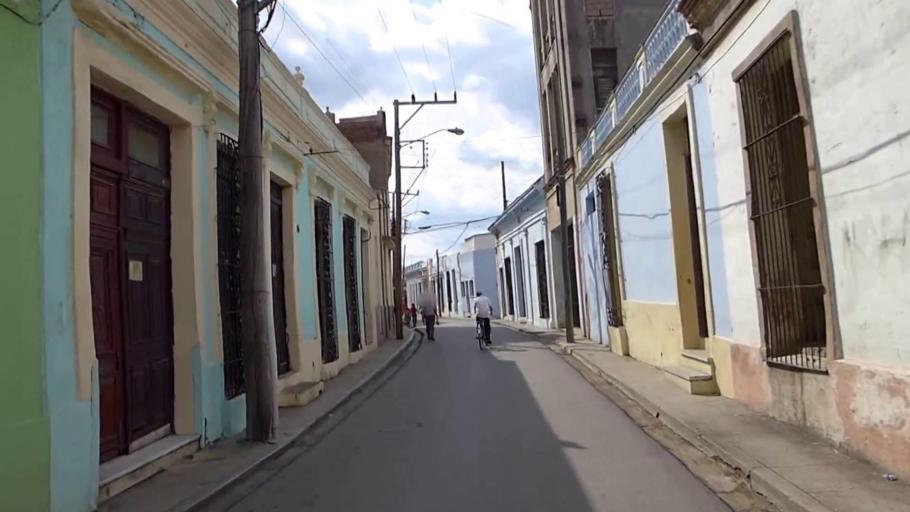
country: CU
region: Camaguey
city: Camaguey
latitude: 21.3831
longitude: -77.9191
